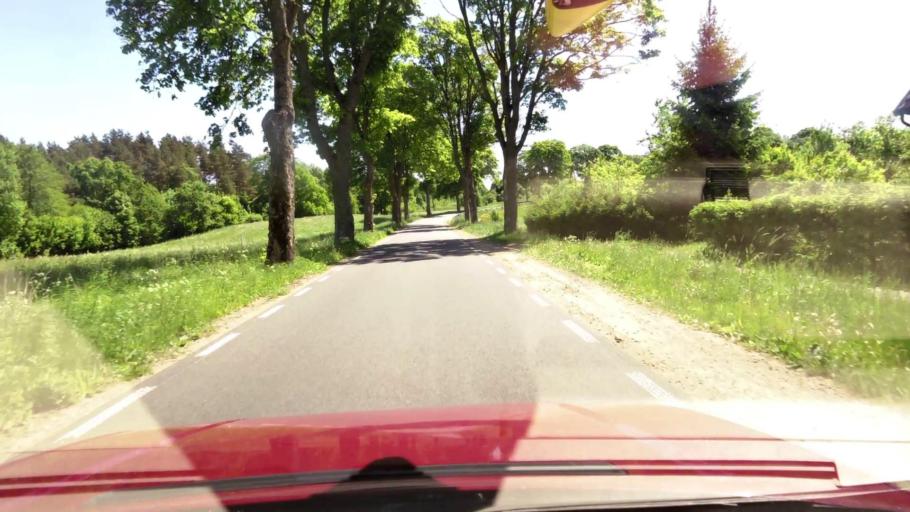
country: PL
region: West Pomeranian Voivodeship
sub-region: Powiat koszalinski
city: Bobolice
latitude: 54.0000
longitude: 16.6807
